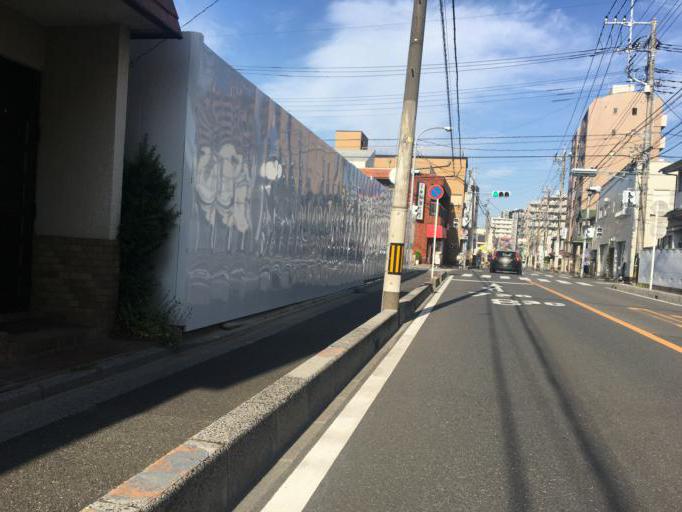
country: JP
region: Saitama
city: Yono
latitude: 35.8636
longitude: 139.6485
